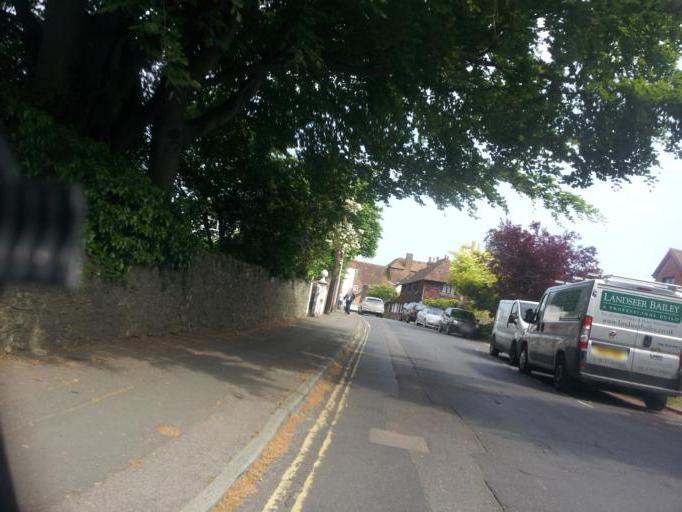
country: GB
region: England
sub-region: Kent
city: West Malling
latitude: 51.2945
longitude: 0.4069
